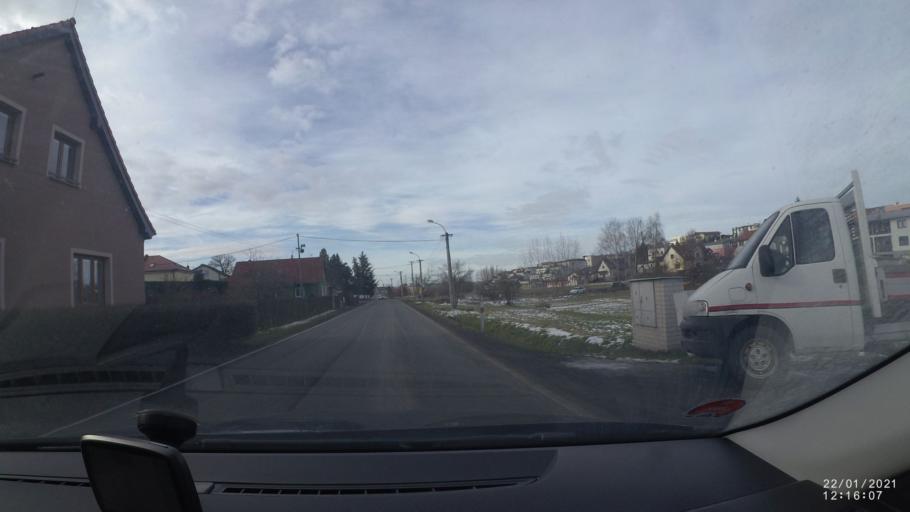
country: CZ
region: Plzensky
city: Dysina
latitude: 49.7564
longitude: 13.4542
